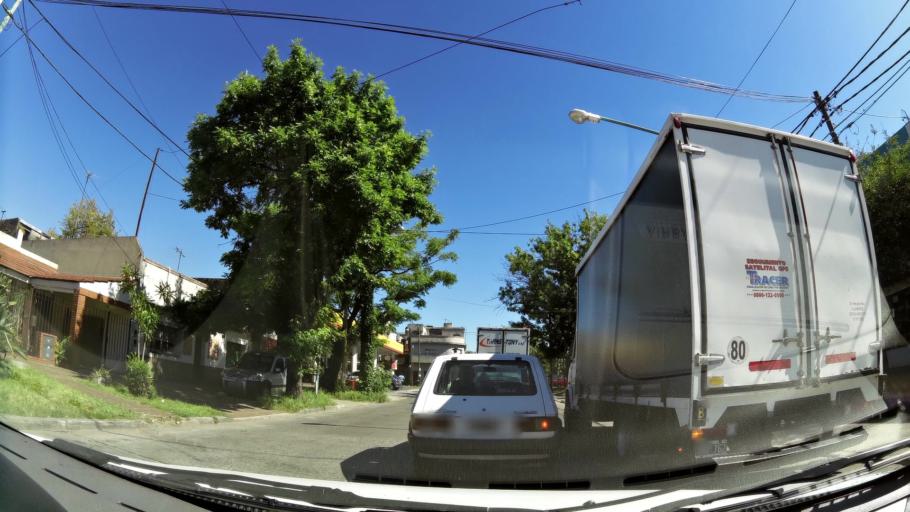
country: AR
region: Buenos Aires
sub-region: Partido de General San Martin
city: General San Martin
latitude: -34.5343
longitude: -58.5314
